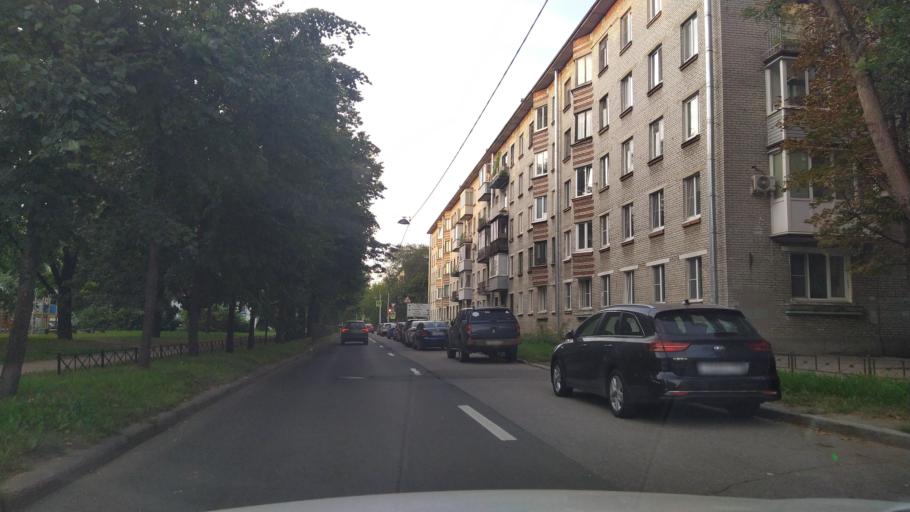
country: RU
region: St.-Petersburg
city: Novaya Derevnya
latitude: 59.9868
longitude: 30.2867
